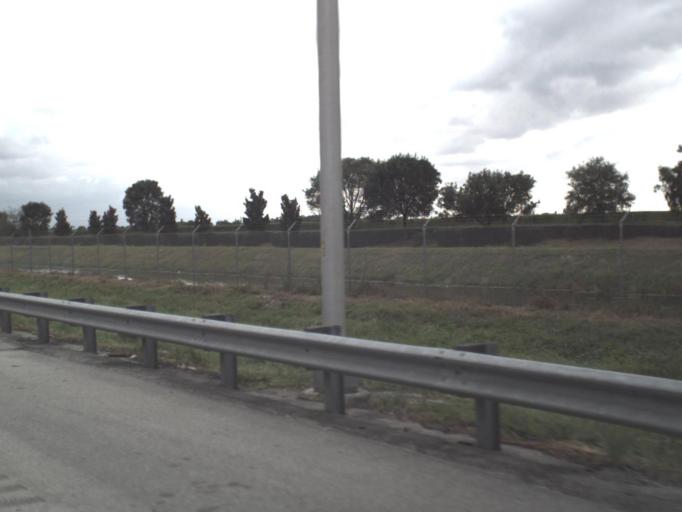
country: US
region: Florida
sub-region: Palm Beach County
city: Seminole Manor
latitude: 26.5473
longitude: -80.1730
